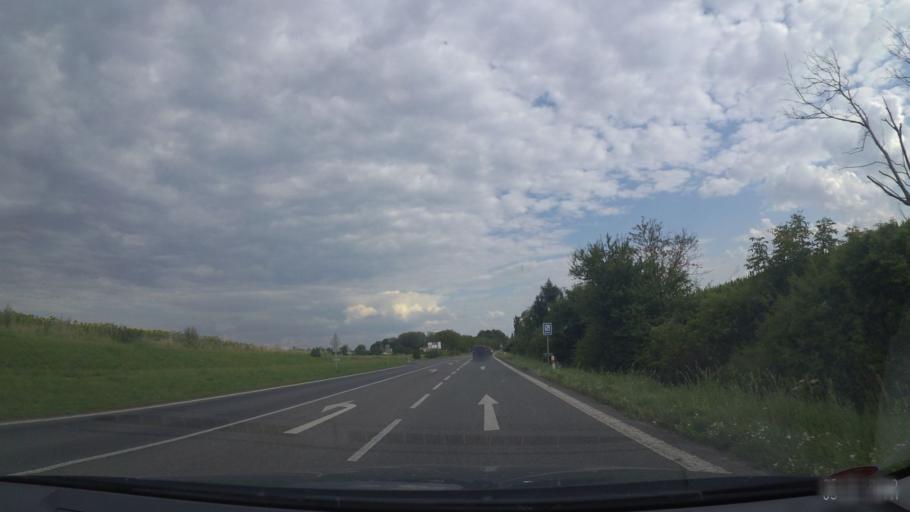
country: CZ
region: Kralovehradecky
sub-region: Okres Hradec Kralove
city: Vsestary
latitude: 50.2627
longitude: 15.7499
